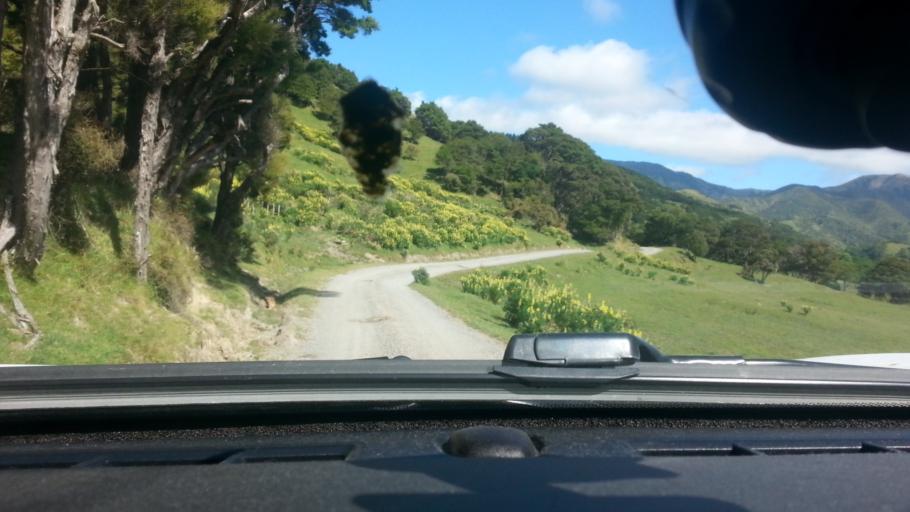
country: NZ
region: Wellington
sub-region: South Wairarapa District
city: Waipawa
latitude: -41.4648
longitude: 175.4259
